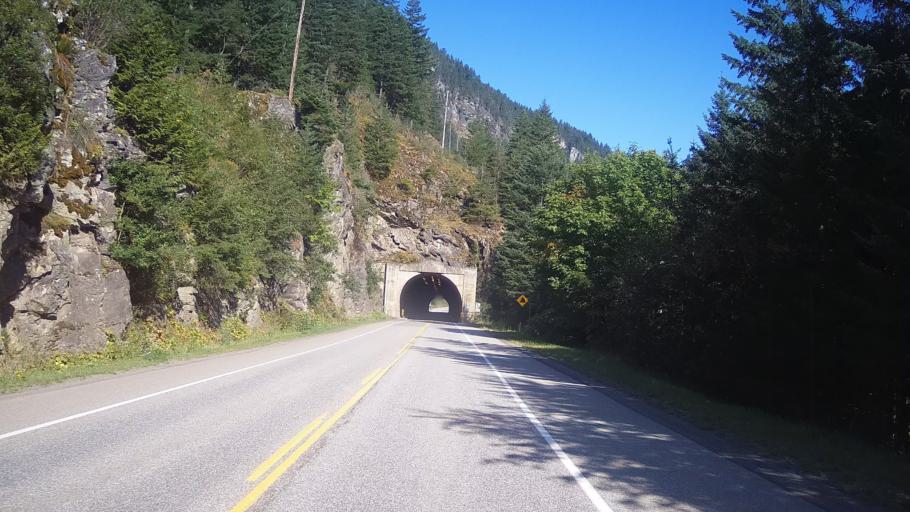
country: CA
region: British Columbia
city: Hope
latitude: 49.6360
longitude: -121.4008
